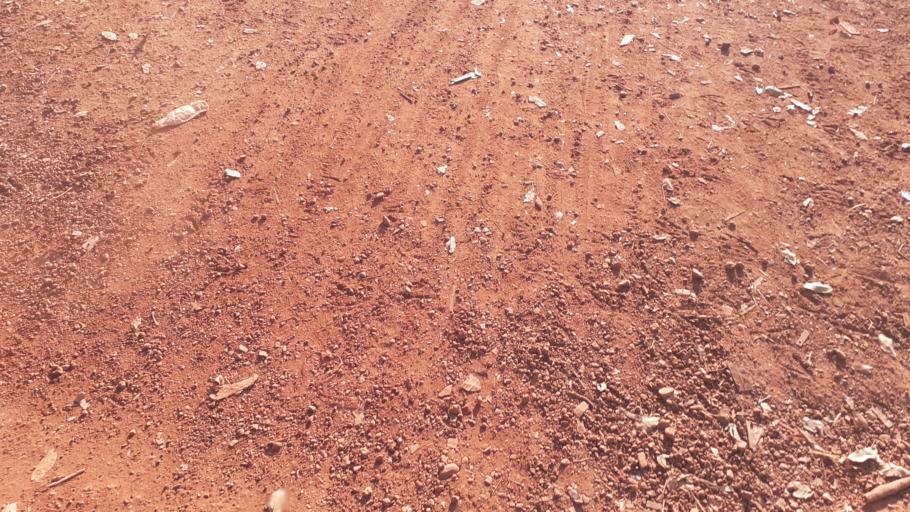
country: GN
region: Kankan
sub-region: Mandiana Prefecture
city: Mandiana
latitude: 10.9304
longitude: -8.8918
